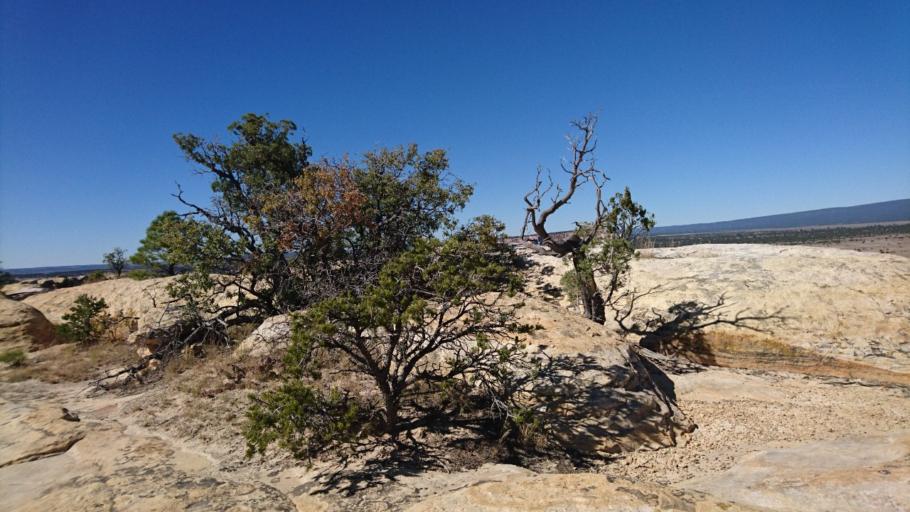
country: US
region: New Mexico
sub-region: McKinley County
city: Thoreau
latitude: 35.0405
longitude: -108.3527
